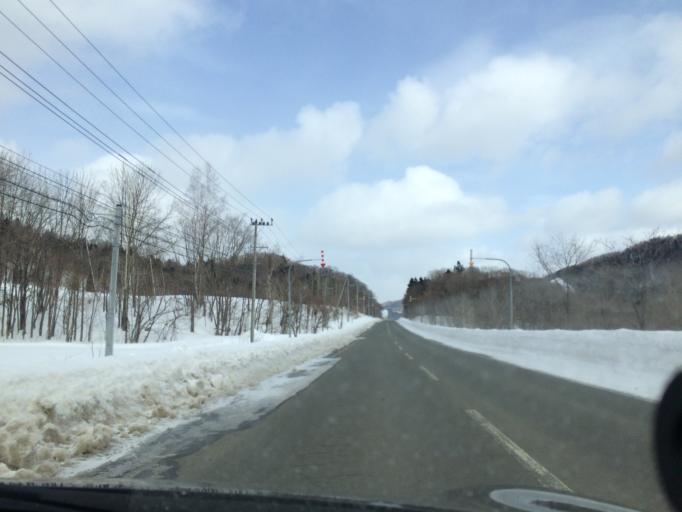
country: JP
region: Hokkaido
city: Shimo-furano
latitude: 43.0135
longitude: 142.4211
